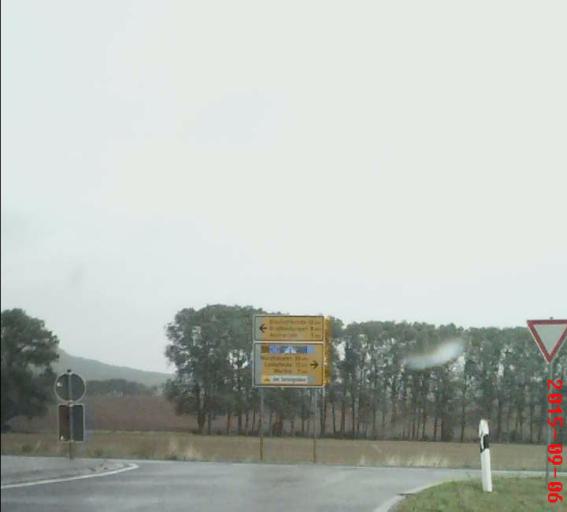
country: DE
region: Thuringia
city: Buhla
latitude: 51.4175
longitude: 10.4328
